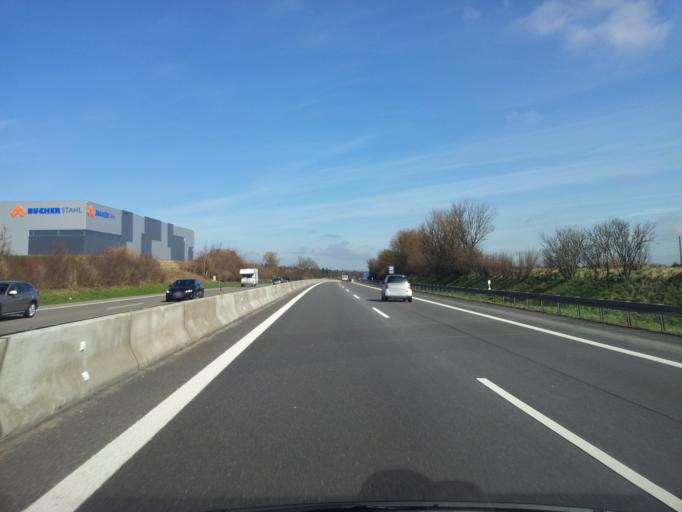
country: DE
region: Baden-Wuerttemberg
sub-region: Freiburg Region
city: Zimmern ob Rottweil
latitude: 48.1647
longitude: 8.5724
